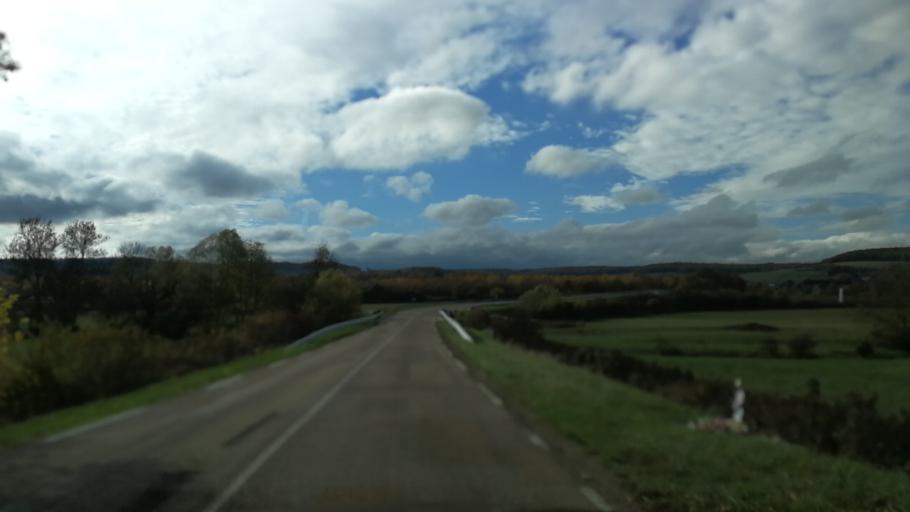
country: FR
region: Bourgogne
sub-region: Departement de la Cote-d'Or
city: Pouilly-en-Auxois
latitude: 47.2744
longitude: 4.5163
